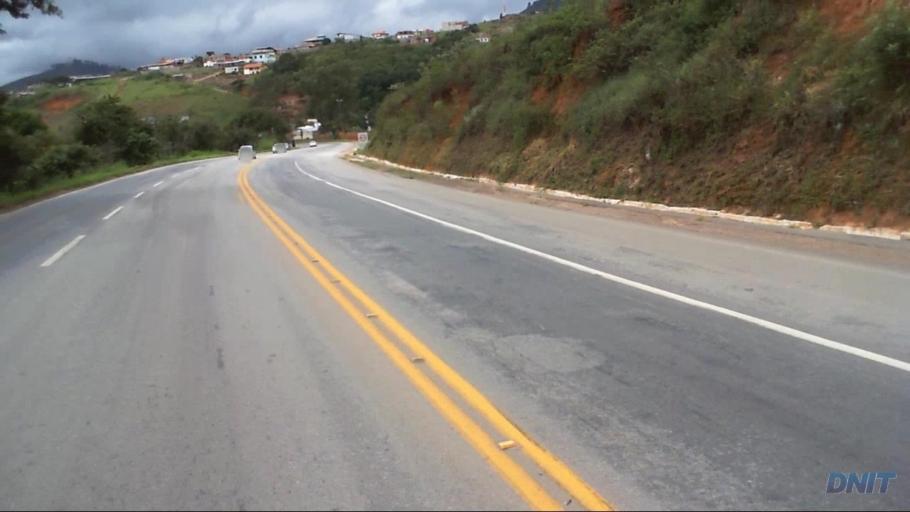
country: BR
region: Minas Gerais
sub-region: Joao Monlevade
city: Joao Monlevade
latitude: -19.8390
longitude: -43.1940
